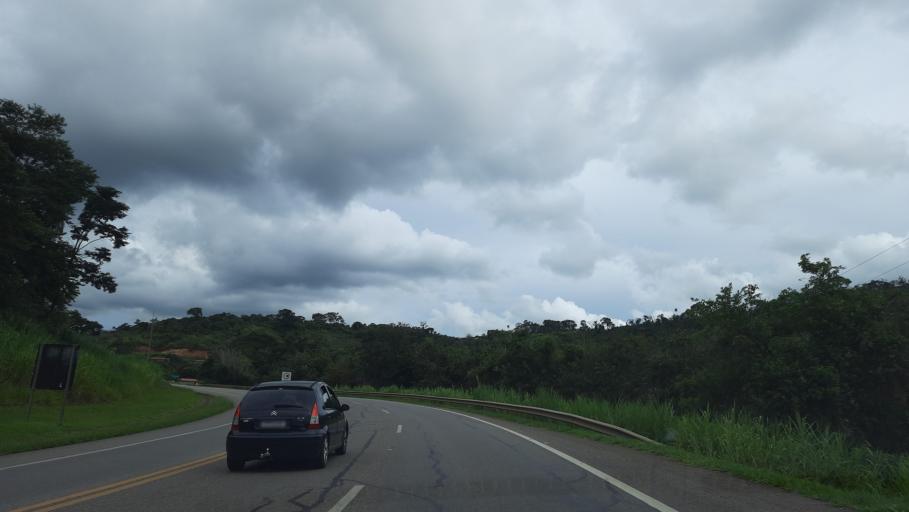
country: BR
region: Sao Paulo
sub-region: Sao Joao Da Boa Vista
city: Sao Joao da Boa Vista
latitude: -21.9367
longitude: -46.7054
